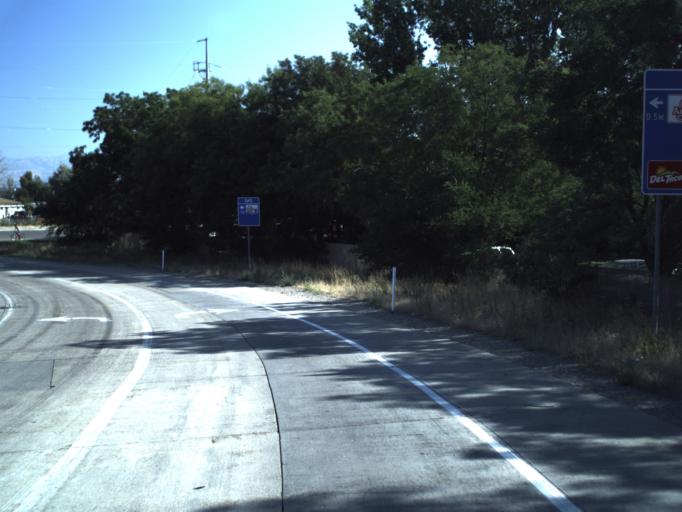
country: US
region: Utah
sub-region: Salt Lake County
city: Taylorsville
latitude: 40.6666
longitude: -111.9501
